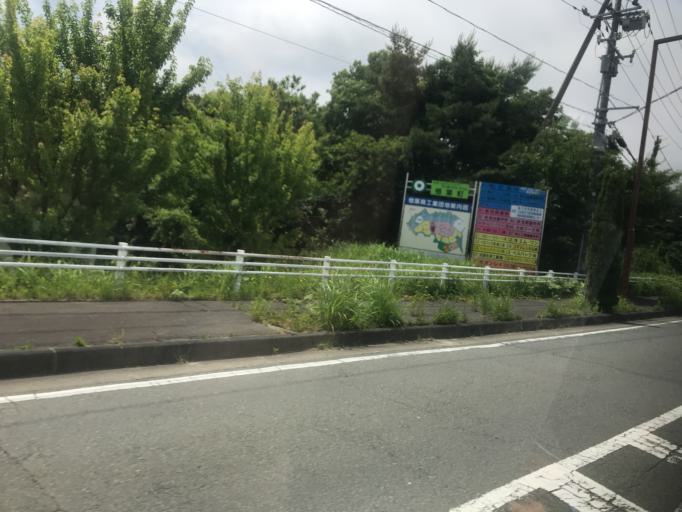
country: JP
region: Fukushima
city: Iwaki
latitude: 37.2437
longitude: 140.9987
